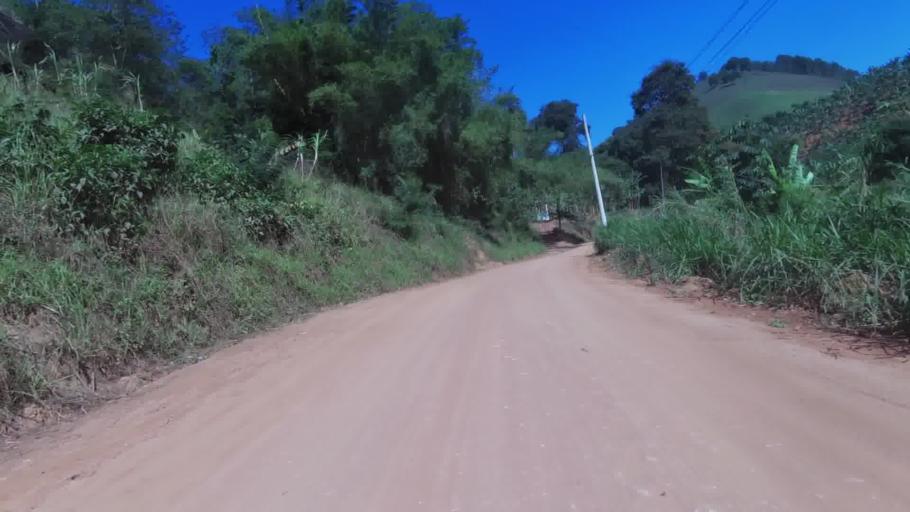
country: BR
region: Espirito Santo
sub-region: Alfredo Chaves
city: Alfredo Chaves
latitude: -20.6452
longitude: -40.7971
